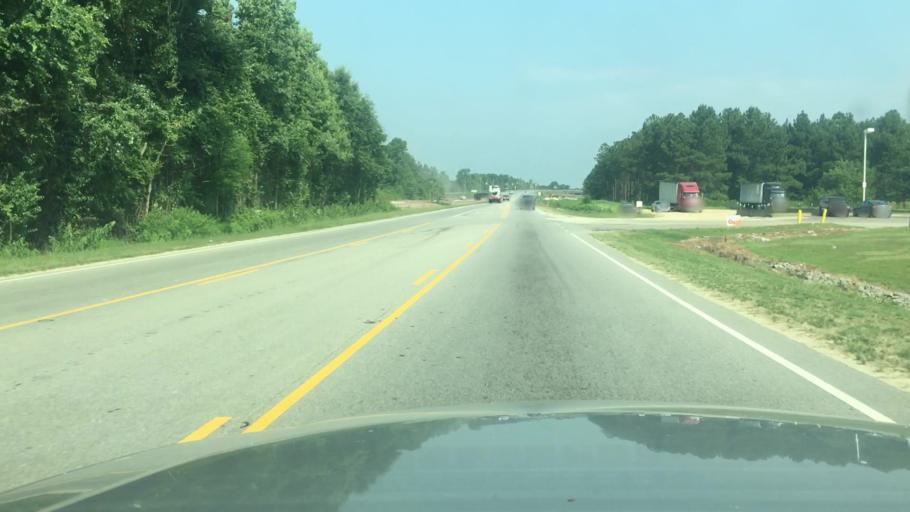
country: US
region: North Carolina
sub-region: Cumberland County
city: Hope Mills
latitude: 34.9412
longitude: -78.9253
